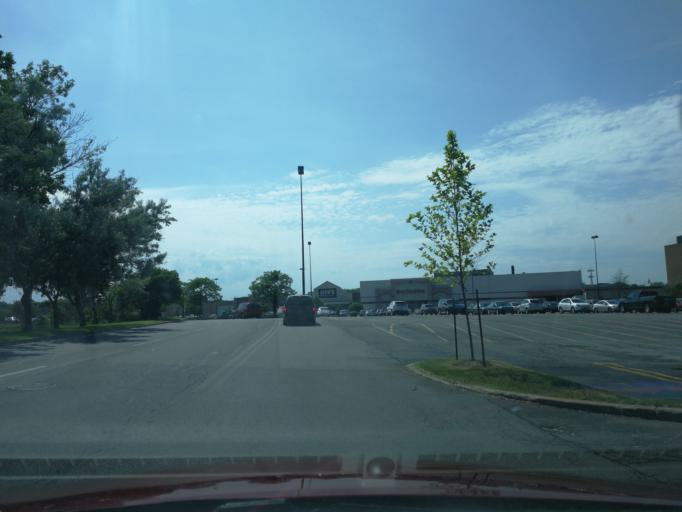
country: US
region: New York
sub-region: Monroe County
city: Greece
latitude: 43.2047
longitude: -77.6902
